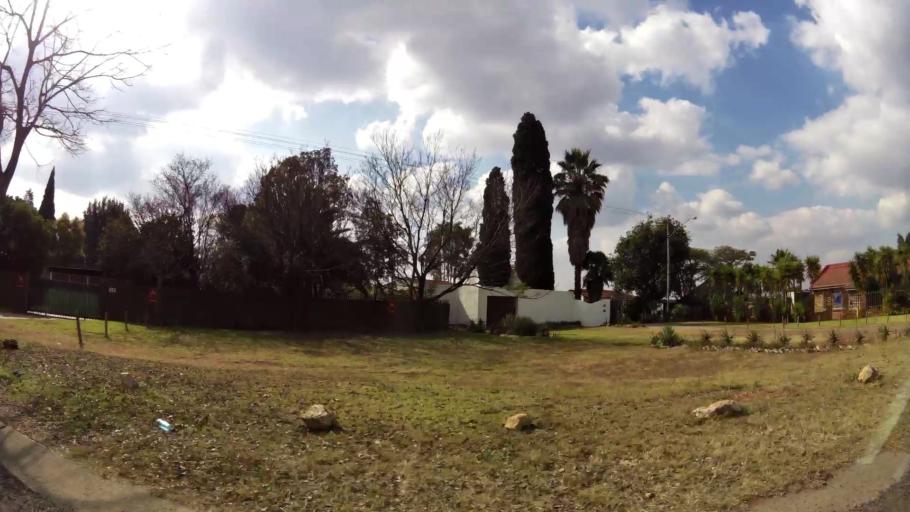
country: ZA
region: Gauteng
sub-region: City of Tshwane Metropolitan Municipality
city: Centurion
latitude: -25.8400
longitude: 28.2708
